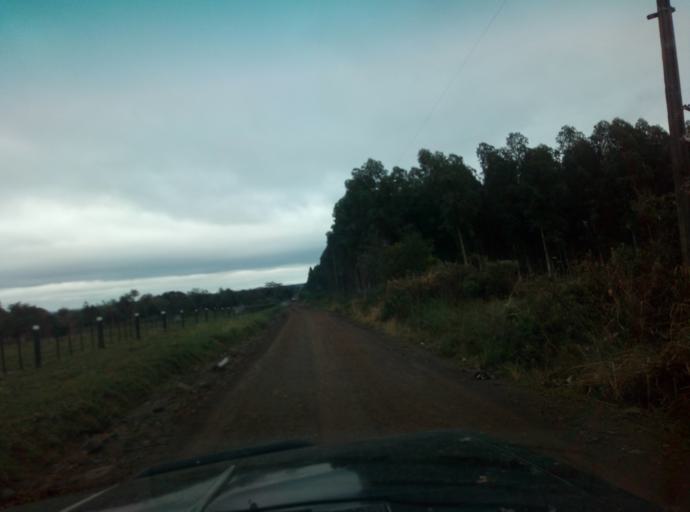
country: PY
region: Caaguazu
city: Carayao
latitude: -25.1902
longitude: -56.3844
